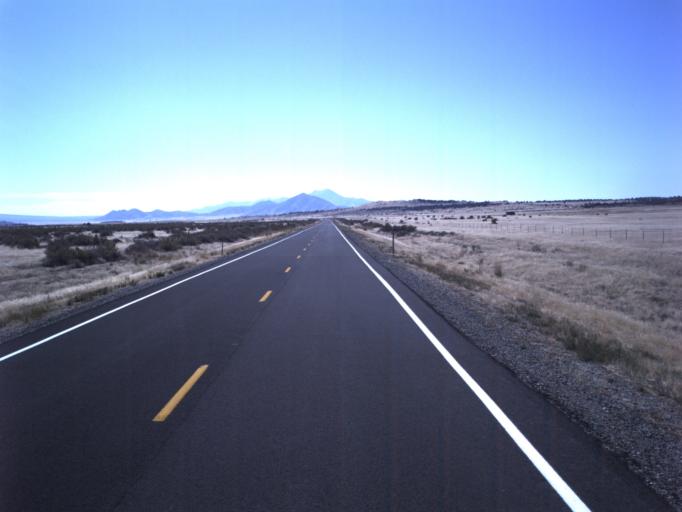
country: US
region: Utah
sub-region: Tooele County
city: Grantsville
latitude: 40.2699
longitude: -112.7413
